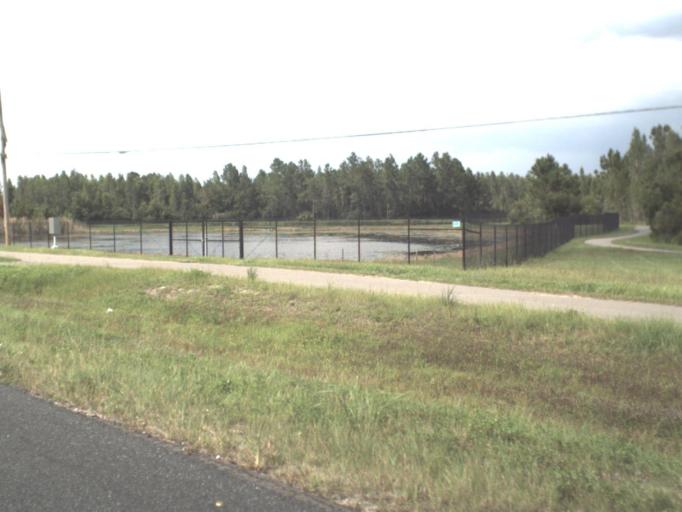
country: US
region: Florida
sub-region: Pasco County
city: Land O' Lakes
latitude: 28.2833
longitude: -82.4857
